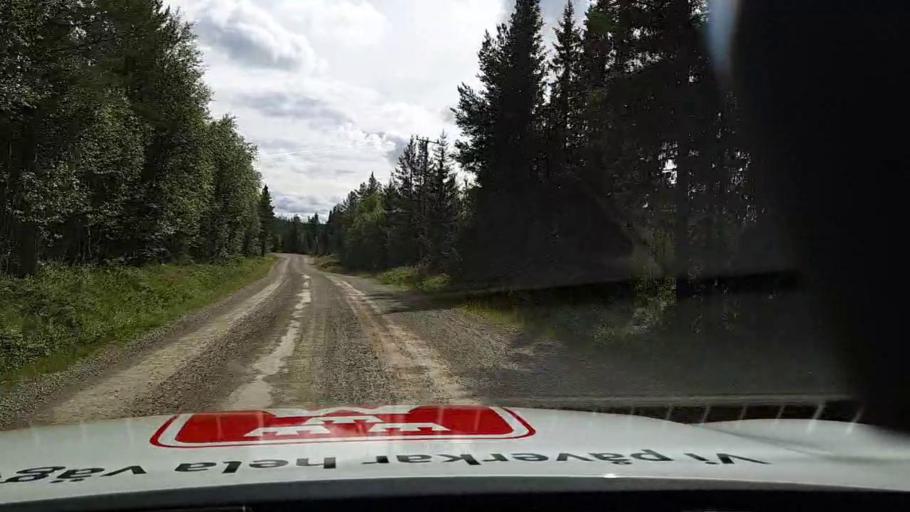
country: SE
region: Jaemtland
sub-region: Are Kommun
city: Jarpen
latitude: 62.5425
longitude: 13.4736
